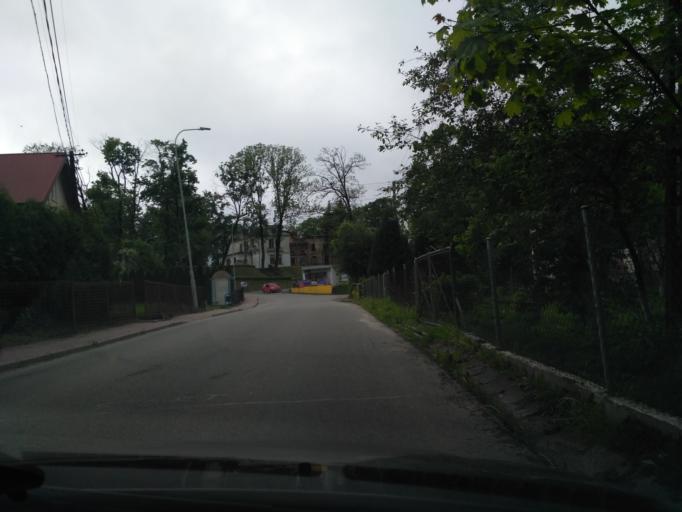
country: PL
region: Subcarpathian Voivodeship
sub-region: Powiat jasielski
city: Brzyska
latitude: 49.8203
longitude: 21.3918
